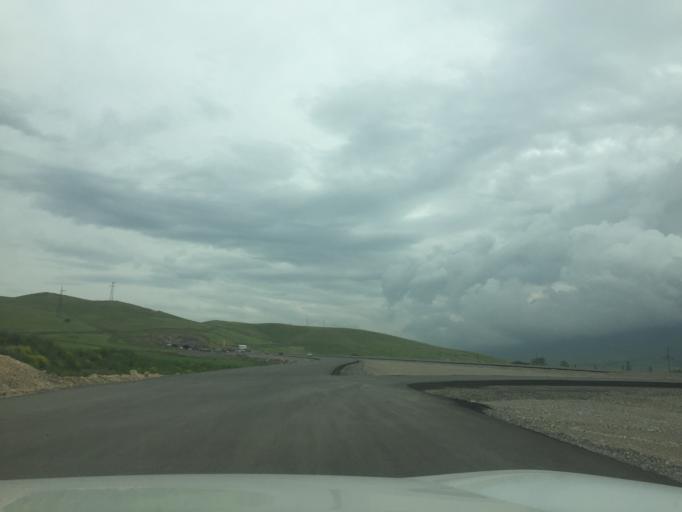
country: KZ
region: Ongtustik Qazaqstan
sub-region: Tulkibas Audany
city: Zhabagly
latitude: 42.5171
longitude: 70.5576
